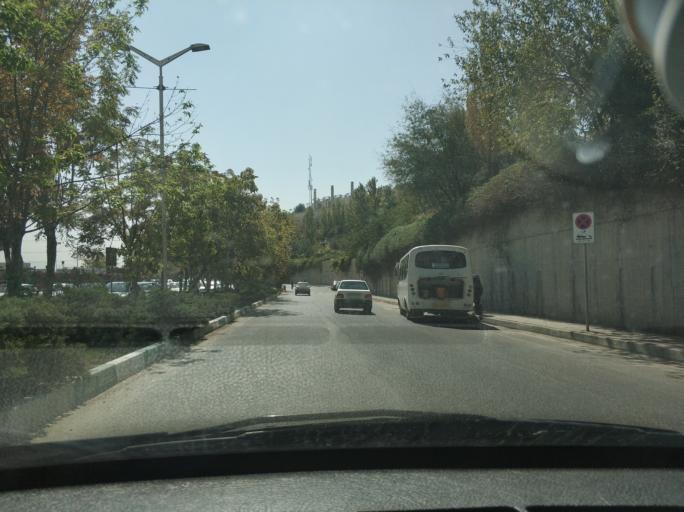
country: IR
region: Tehran
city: Tehran
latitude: 35.7472
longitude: 51.3786
